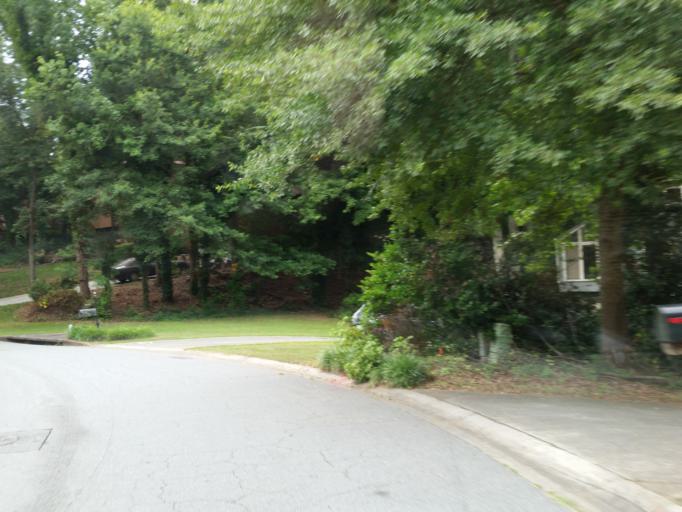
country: US
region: Georgia
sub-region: Cherokee County
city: Woodstock
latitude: 34.0173
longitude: -84.4765
